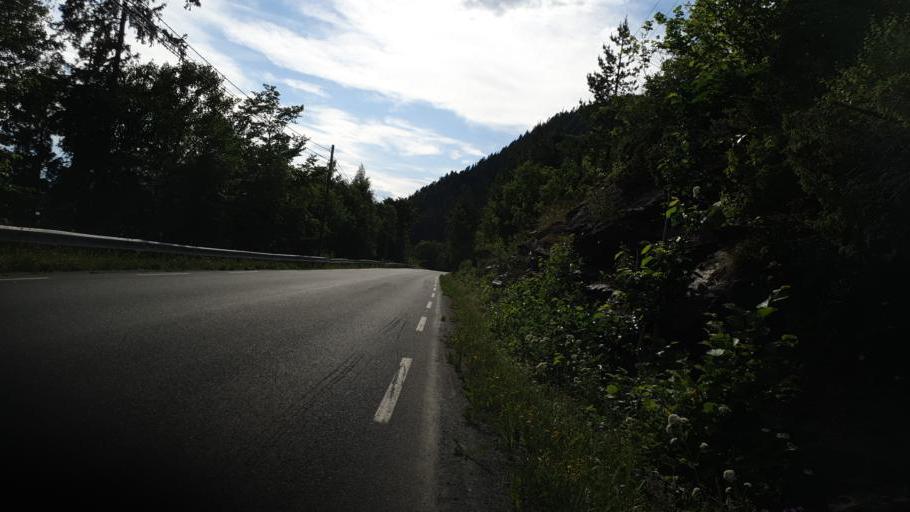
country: NO
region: Sor-Trondelag
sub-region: Trondheim
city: Trondheim
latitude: 63.5576
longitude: 10.2774
